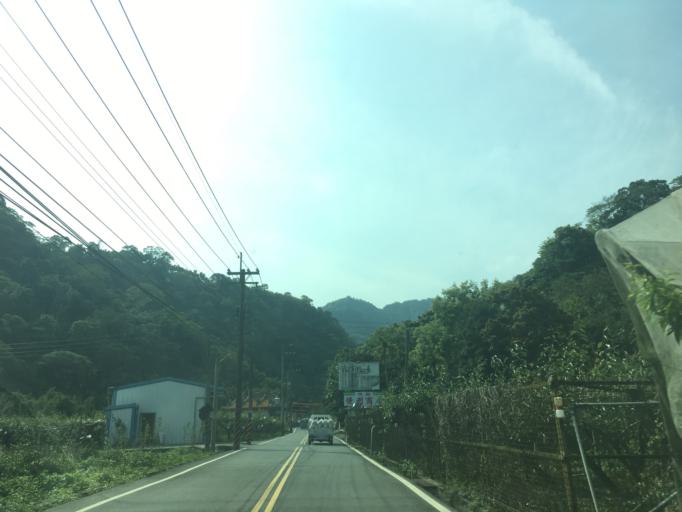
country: TW
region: Taiwan
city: Fengyuan
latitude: 24.1641
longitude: 120.8254
